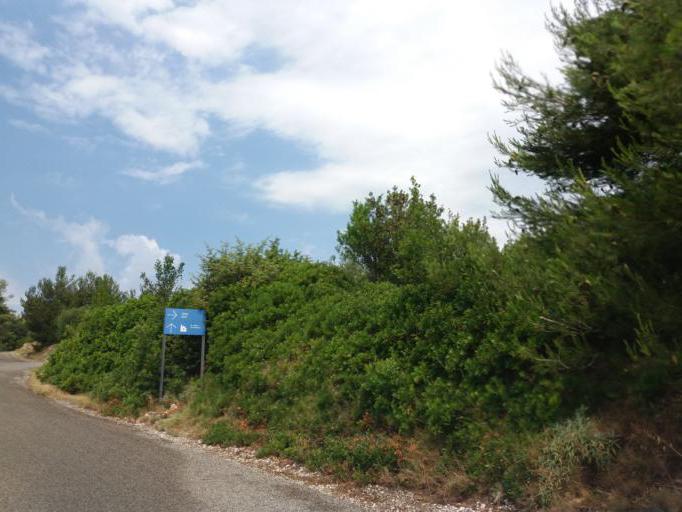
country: HR
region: Zadarska
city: Sali
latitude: 43.9268
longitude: 15.1353
